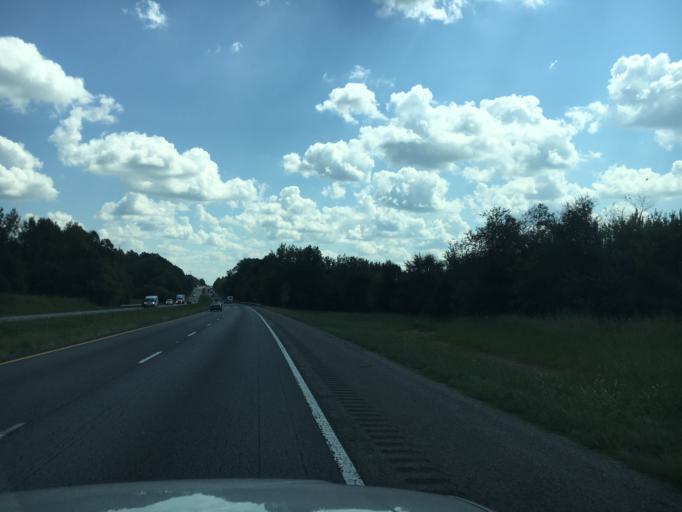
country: US
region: South Carolina
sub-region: Spartanburg County
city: Roebuck
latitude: 34.8682
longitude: -81.9871
